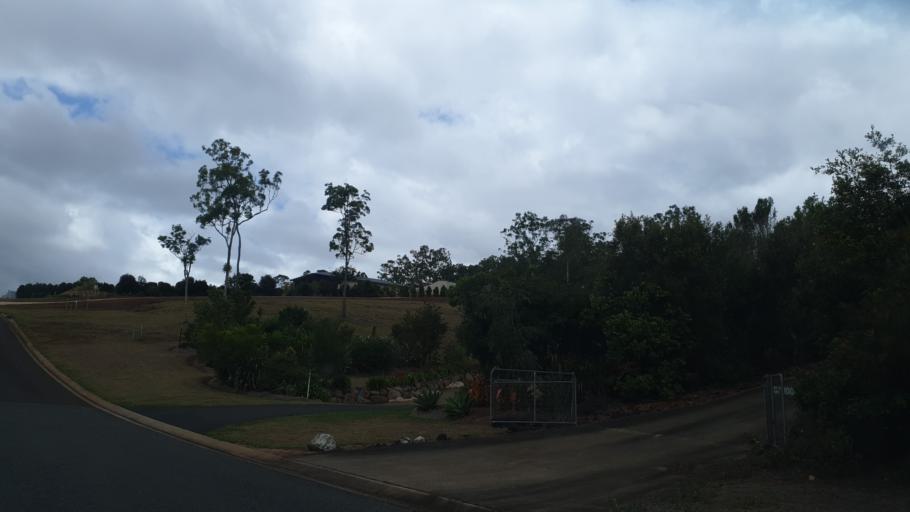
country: AU
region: Queensland
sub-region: Tablelands
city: Tolga
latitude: -17.2130
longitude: 145.4476
